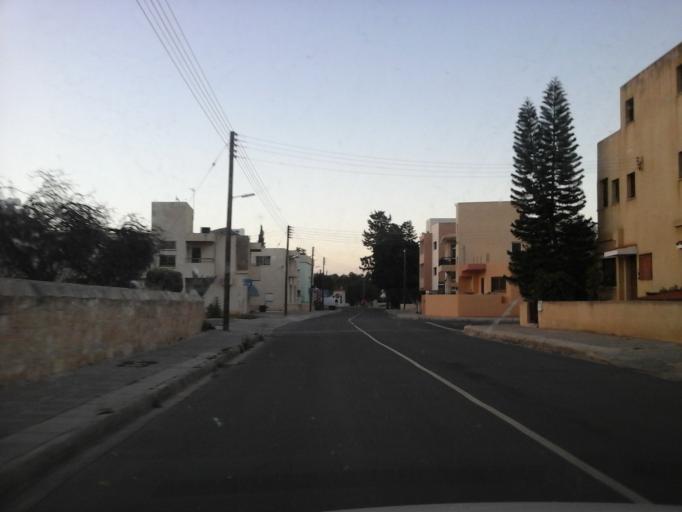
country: CY
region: Pafos
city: Paphos
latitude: 34.7638
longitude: 32.4539
